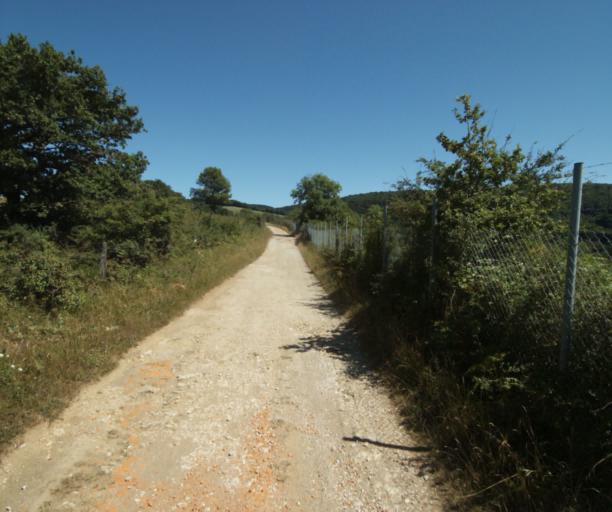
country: FR
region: Midi-Pyrenees
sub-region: Departement du Tarn
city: Soreze
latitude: 43.4439
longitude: 2.0889
